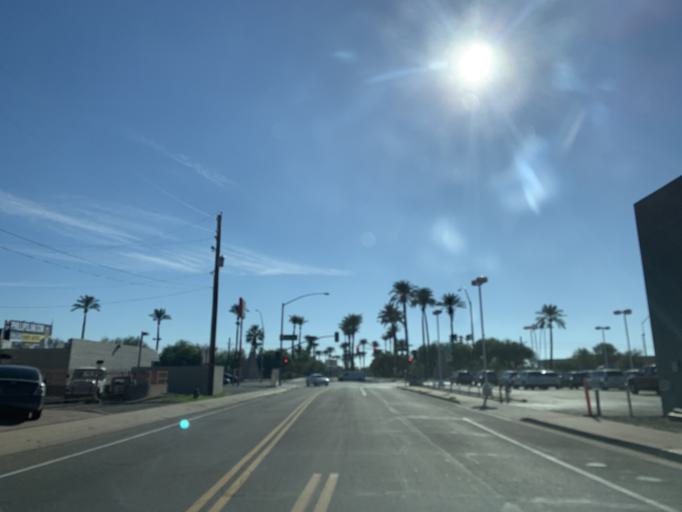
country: US
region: Arizona
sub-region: Maricopa County
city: Mesa
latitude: 33.4156
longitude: -111.8654
